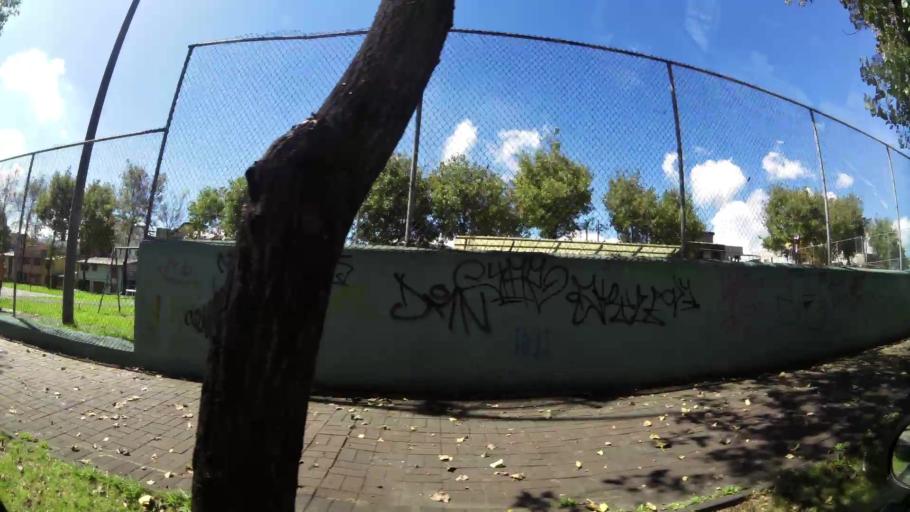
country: EC
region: Pichincha
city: Quito
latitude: -0.2564
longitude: -78.5327
